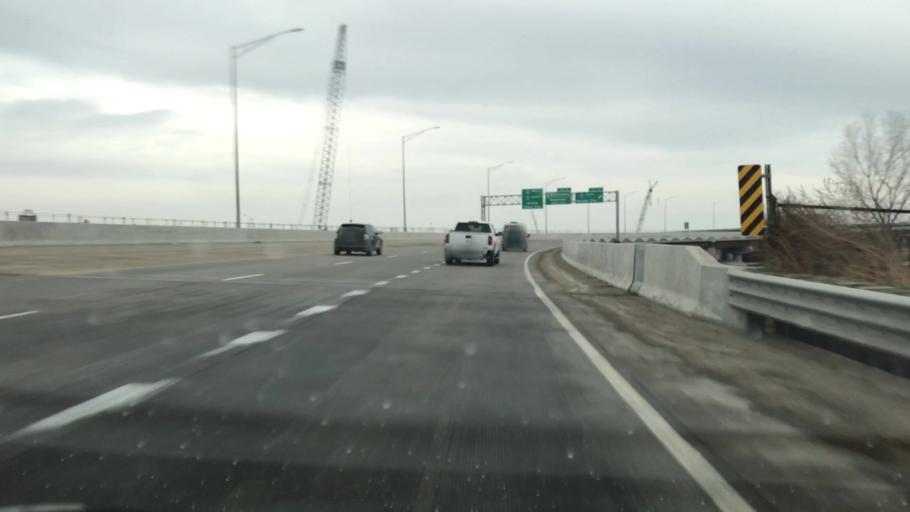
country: US
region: Iowa
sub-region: Pottawattamie County
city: Council Bluffs
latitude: 41.2326
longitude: -95.8306
